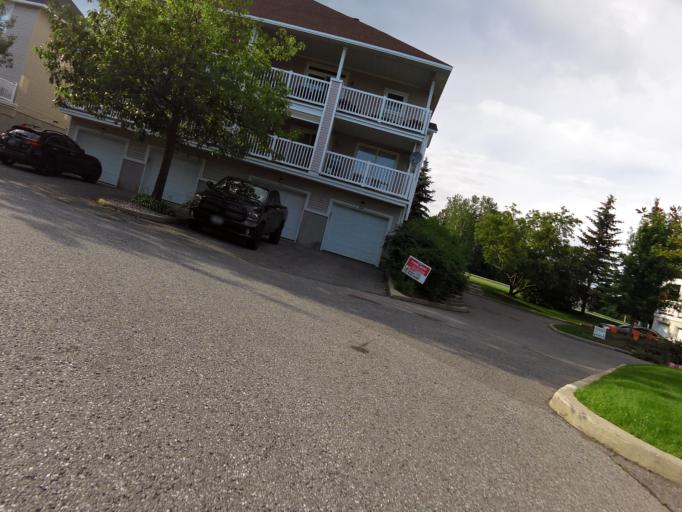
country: CA
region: Ontario
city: Bells Corners
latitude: 45.3218
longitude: -75.8914
